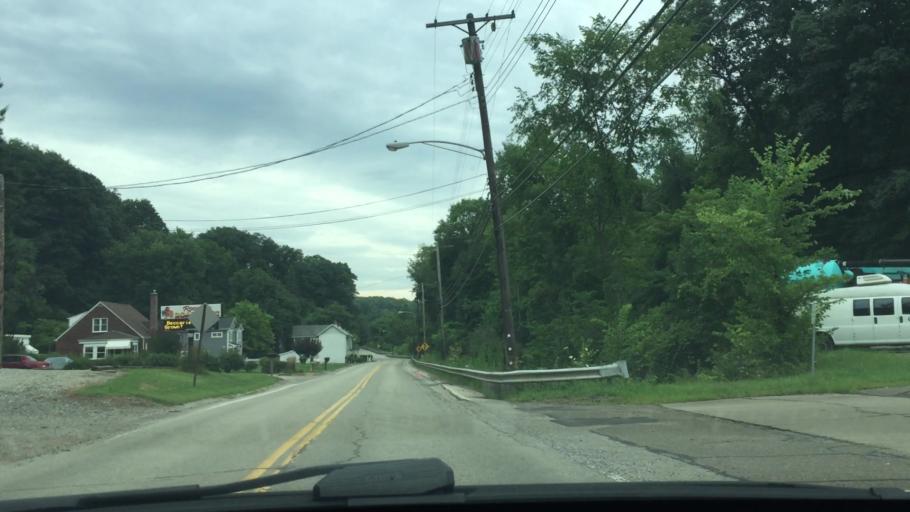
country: US
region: Pennsylvania
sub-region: Allegheny County
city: Rennerdale
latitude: 40.3786
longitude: -80.1467
